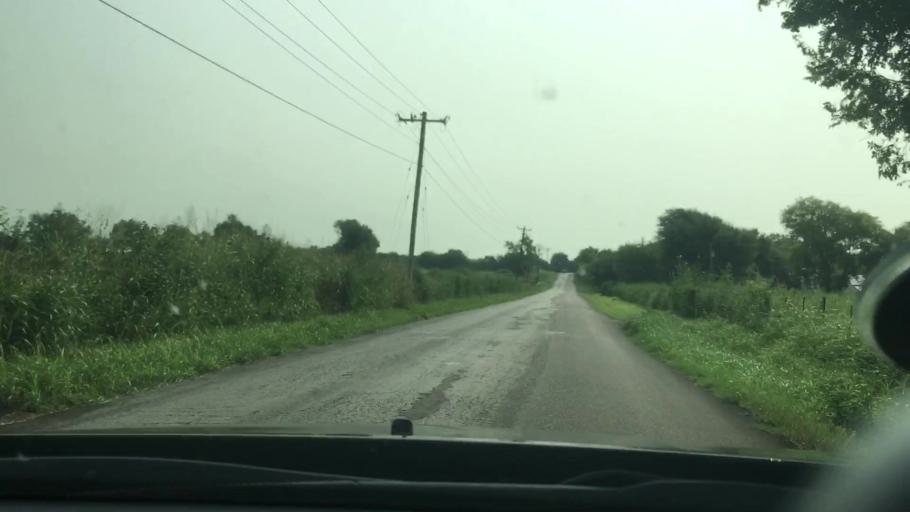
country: US
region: Oklahoma
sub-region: Garvin County
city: Lindsay
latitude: 34.8101
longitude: -97.6134
